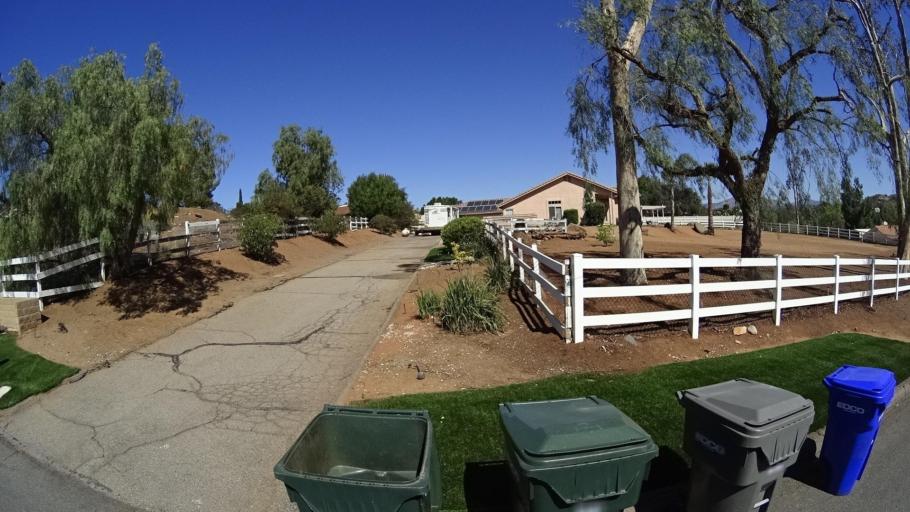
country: US
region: California
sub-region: San Diego County
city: Alpine
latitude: 32.8136
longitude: -116.7831
